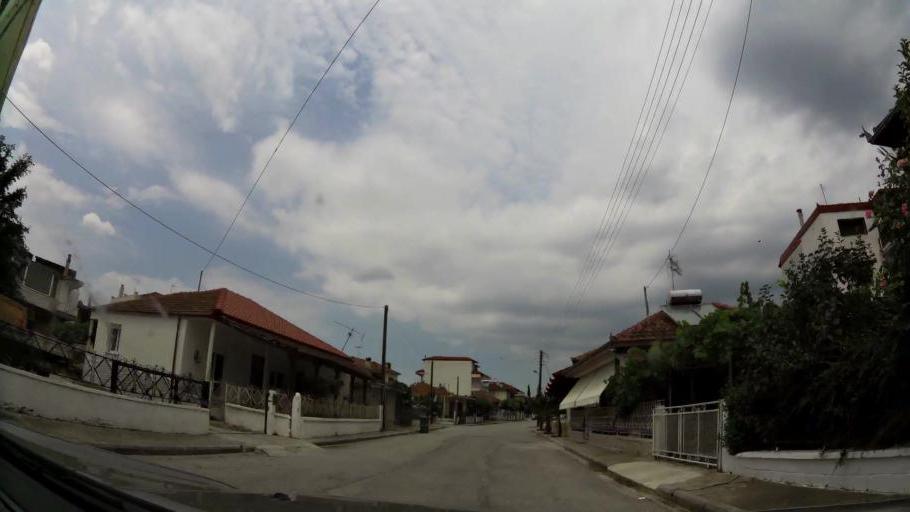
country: GR
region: Central Macedonia
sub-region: Nomos Pierias
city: Kallithea
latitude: 40.2741
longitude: 22.5789
